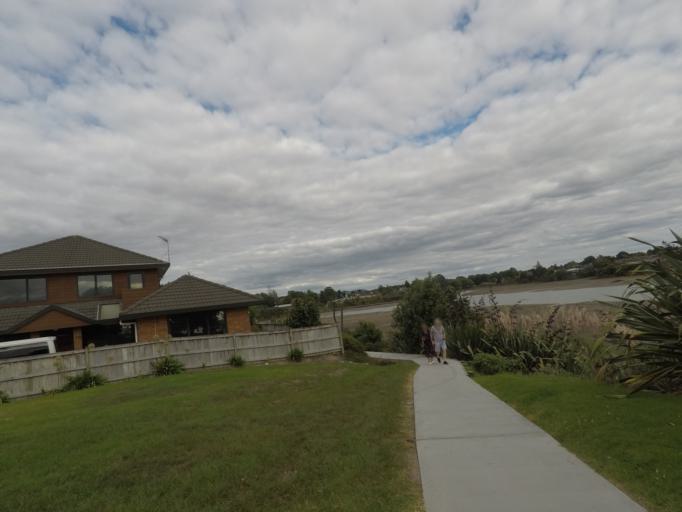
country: NZ
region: Auckland
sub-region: Auckland
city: Papakura
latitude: -37.0601
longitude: 174.9308
